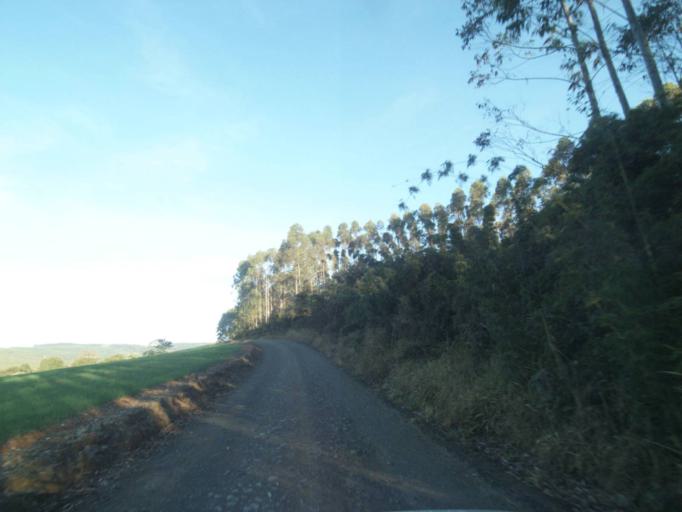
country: BR
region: Parana
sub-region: Telemaco Borba
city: Telemaco Borba
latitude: -24.4385
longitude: -50.6019
